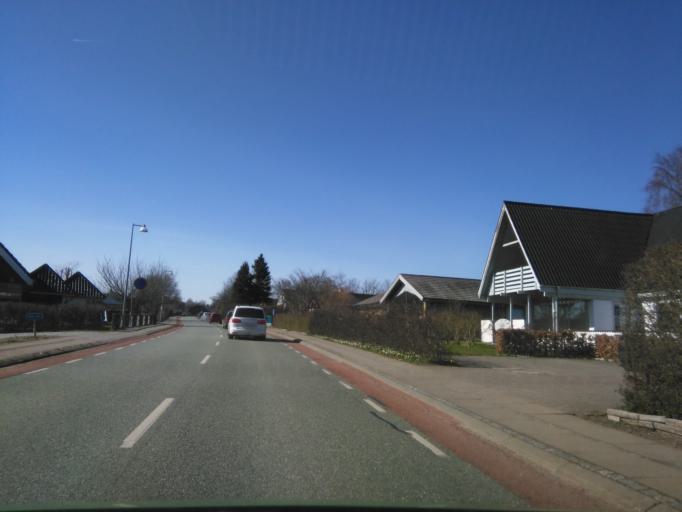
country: DK
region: Central Jutland
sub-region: Favrskov Kommune
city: Hinnerup
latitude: 56.2492
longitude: 10.0337
